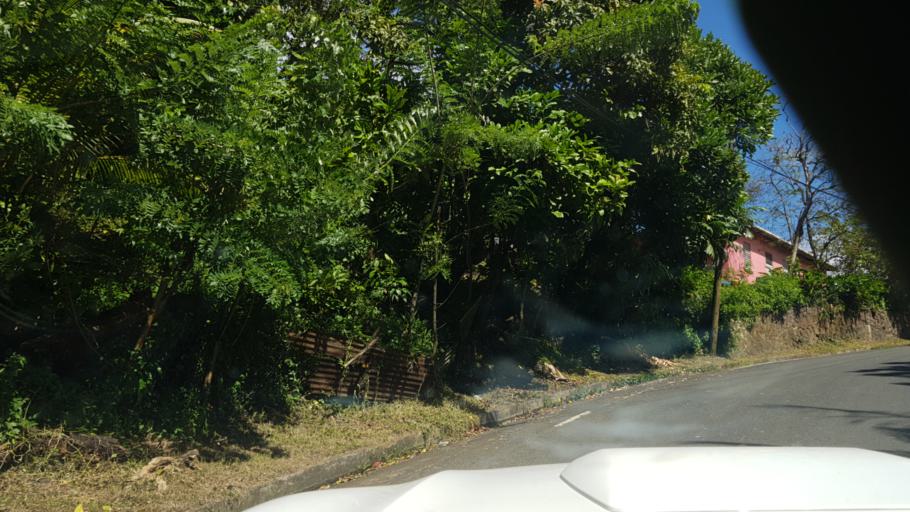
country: LC
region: Castries Quarter
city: Castries
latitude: 13.9838
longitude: -60.9731
